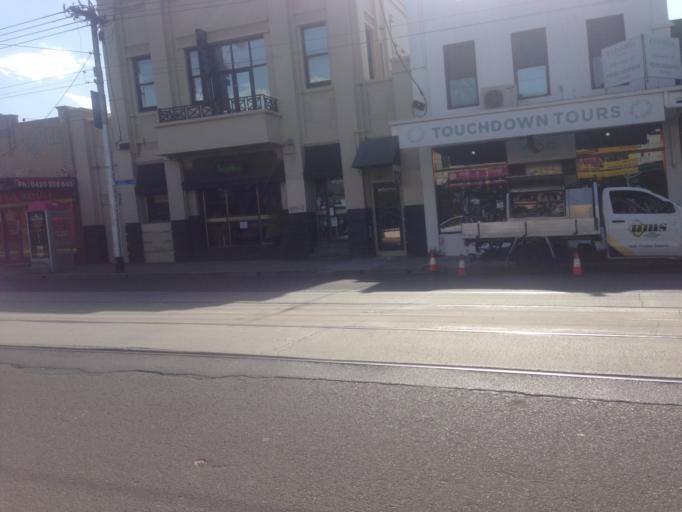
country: AU
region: Victoria
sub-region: Darebin
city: Northcote
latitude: -37.7654
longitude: 144.9995
